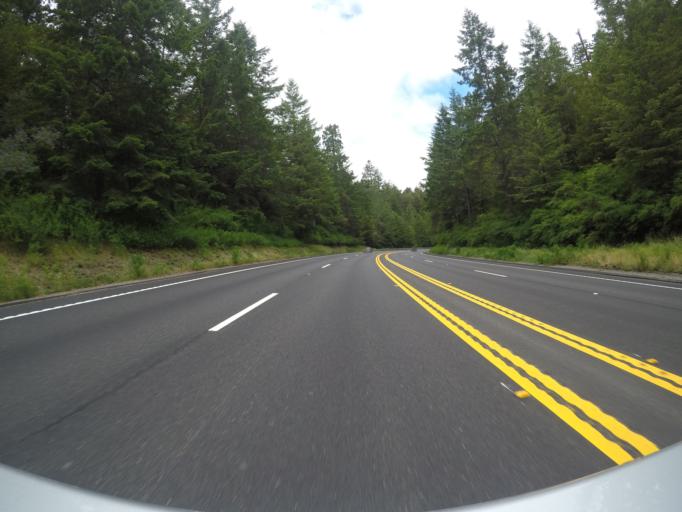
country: US
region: California
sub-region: Humboldt County
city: Rio Dell
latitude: 40.3391
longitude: -123.9342
